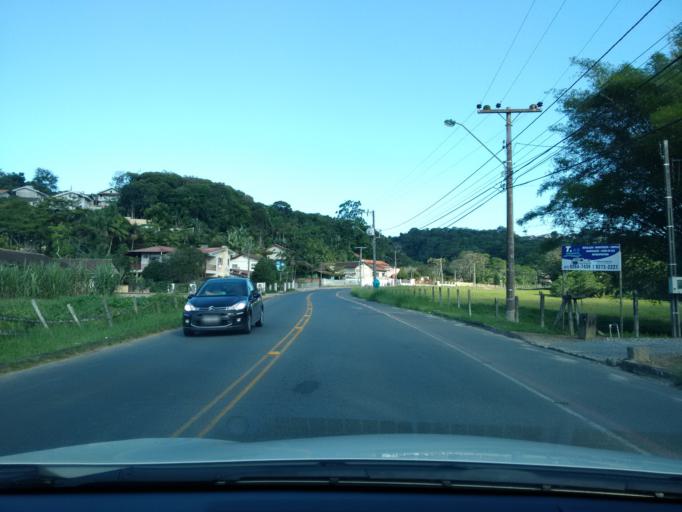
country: BR
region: Santa Catarina
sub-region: Blumenau
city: Blumenau
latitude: -26.8524
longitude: -49.0801
